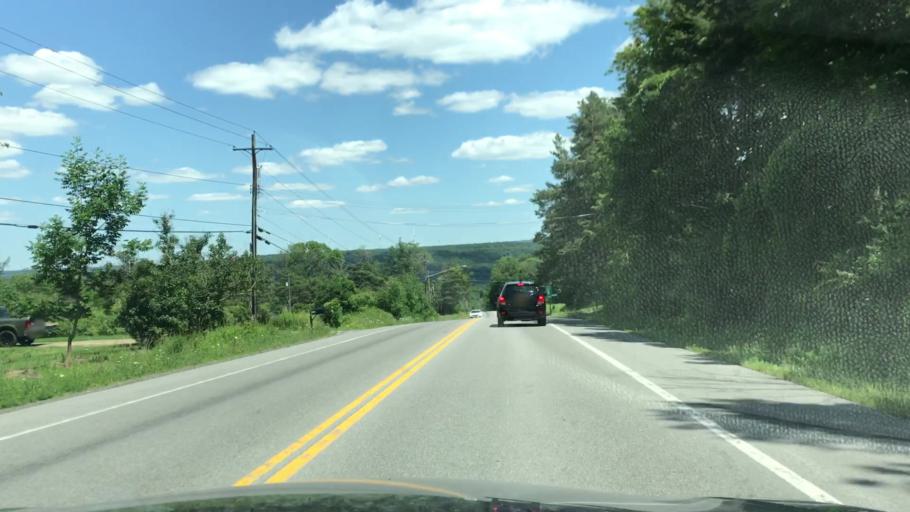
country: US
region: New York
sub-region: Wyoming County
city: Attica
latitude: 42.7704
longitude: -78.3389
